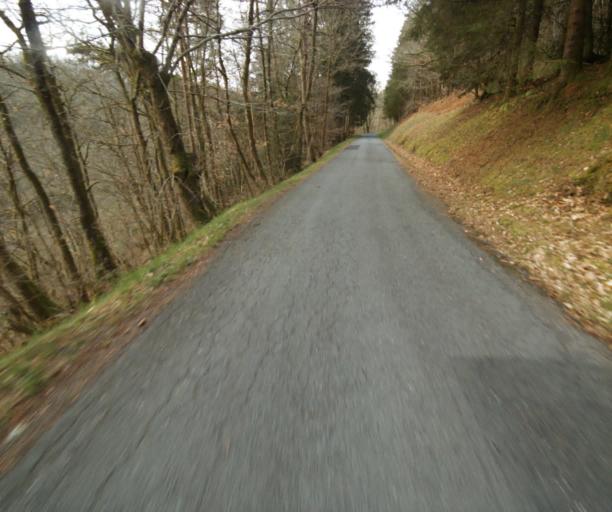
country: FR
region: Limousin
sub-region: Departement de la Correze
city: Correze
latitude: 45.3872
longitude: 1.8893
